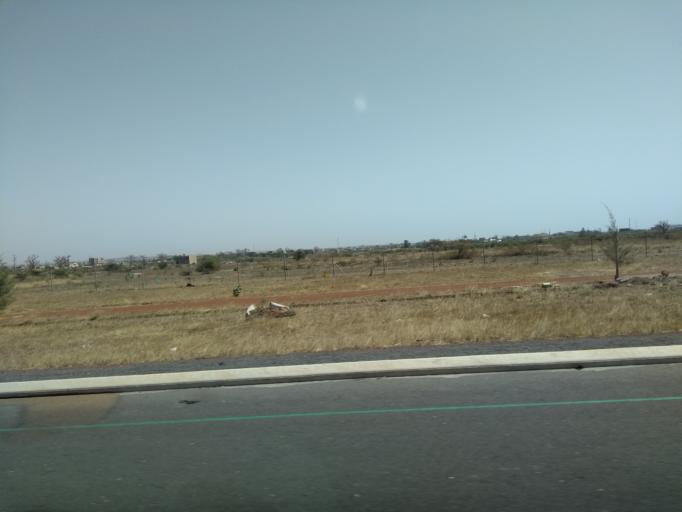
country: SN
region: Thies
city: Thies
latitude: 14.7392
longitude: -17.1910
